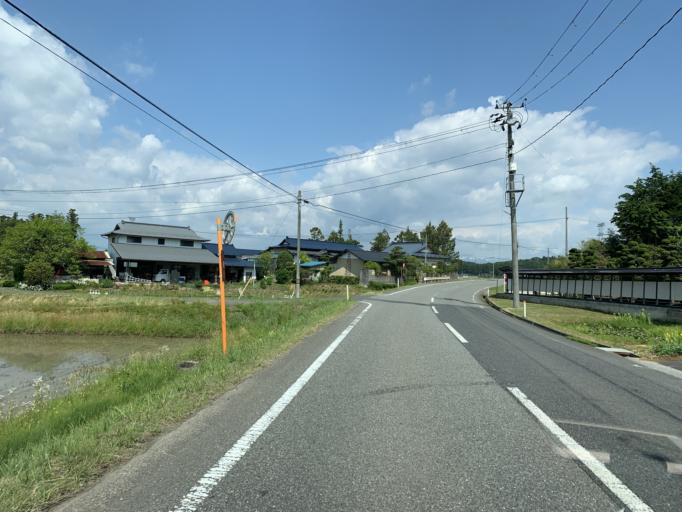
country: JP
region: Iwate
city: Ichinoseki
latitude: 38.7981
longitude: 141.0174
